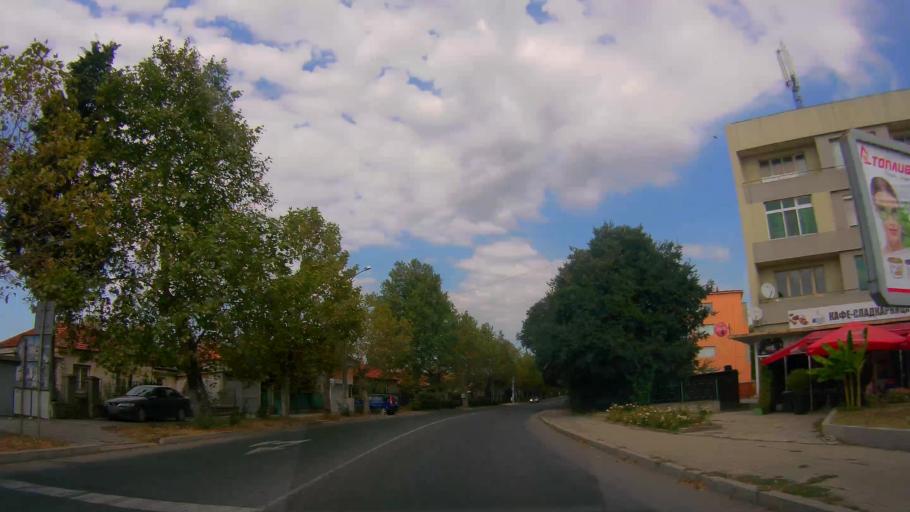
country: BG
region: Burgas
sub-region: Obshtina Aytos
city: Aytos
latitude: 42.6992
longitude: 27.2487
